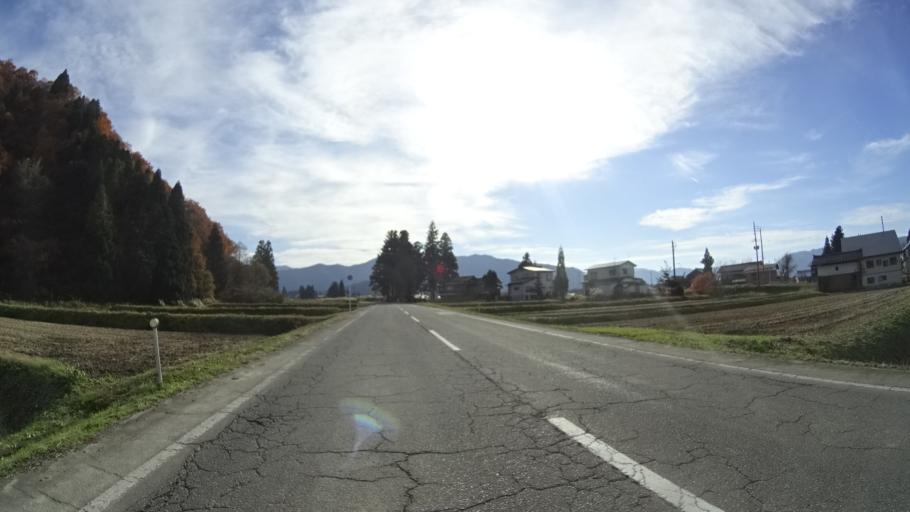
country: JP
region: Niigata
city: Shiozawa
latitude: 37.0248
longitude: 138.8811
